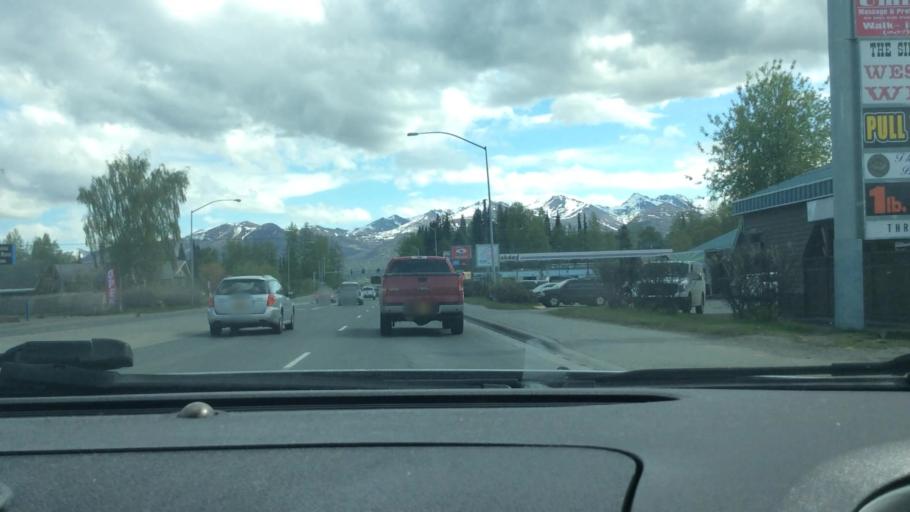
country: US
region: Alaska
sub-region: Anchorage Municipality
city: Anchorage
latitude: 61.1807
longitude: -149.8291
